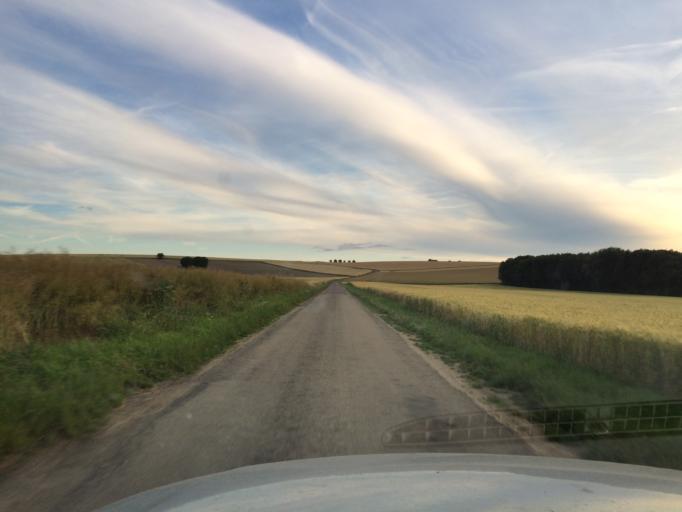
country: FR
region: Bourgogne
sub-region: Departement de l'Yonne
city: Aillant-sur-Tholon
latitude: 47.8616
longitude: 3.3864
